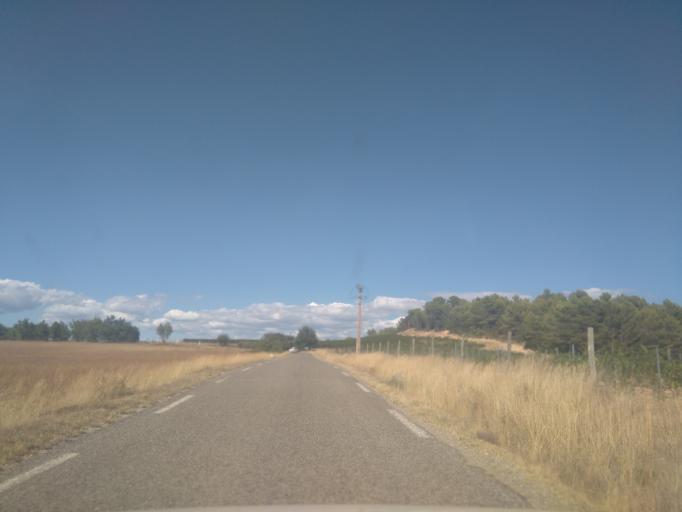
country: FR
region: Provence-Alpes-Cote d'Azur
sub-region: Departement du Var
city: Regusse
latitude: 43.6967
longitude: 6.1195
